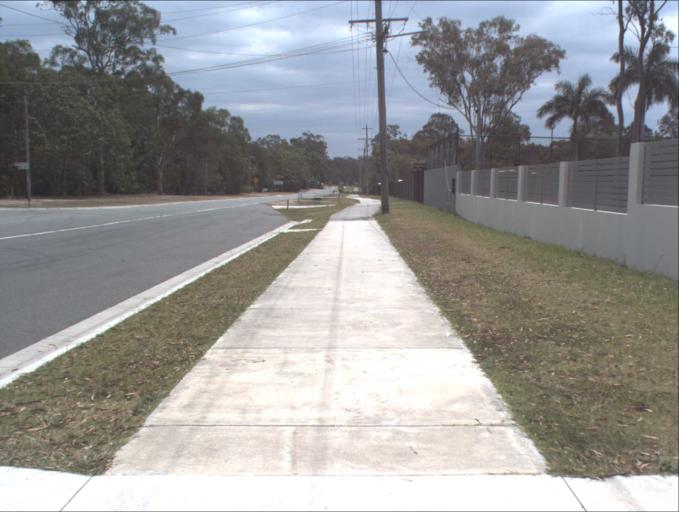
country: AU
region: Queensland
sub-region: Logan
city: Beenleigh
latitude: -27.6661
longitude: 153.2180
